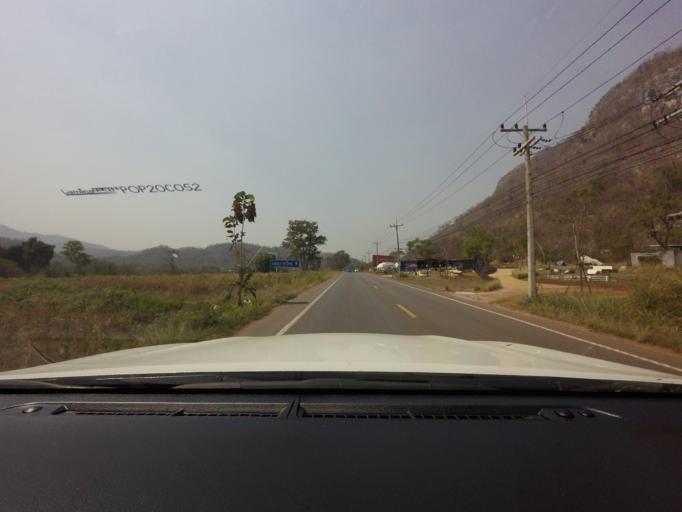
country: TH
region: Sara Buri
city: Muak Lek
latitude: 14.5549
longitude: 101.3136
